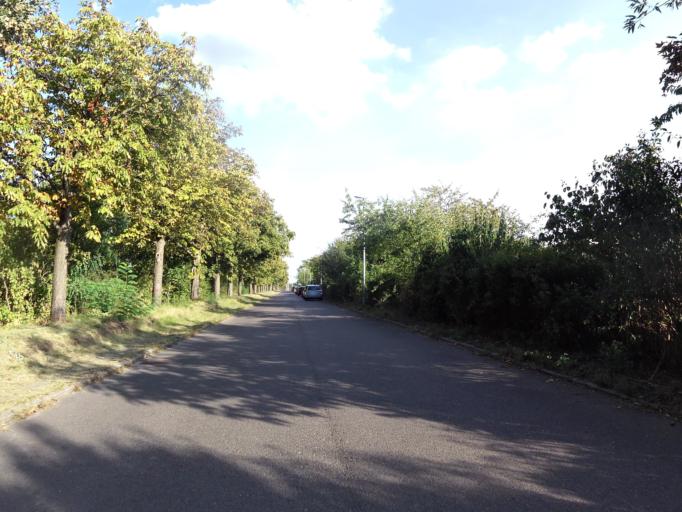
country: DE
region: Saxony
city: Schkeuditz
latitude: 51.3540
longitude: 12.2613
